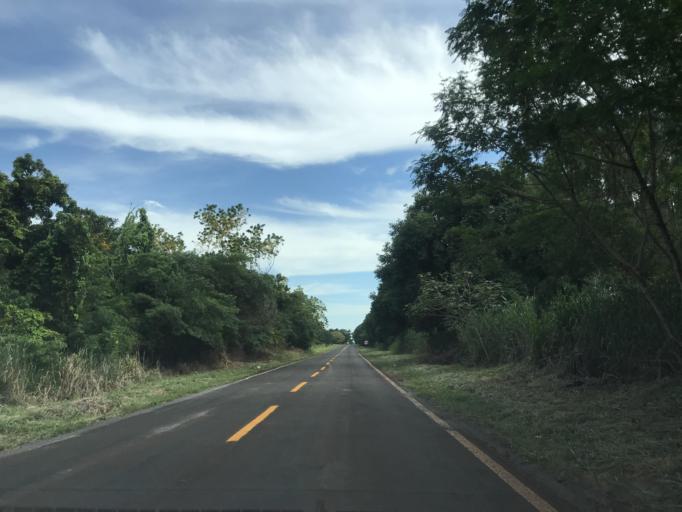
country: BR
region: Parana
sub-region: Terra Rica
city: Terra Rica
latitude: -22.7912
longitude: -52.6540
